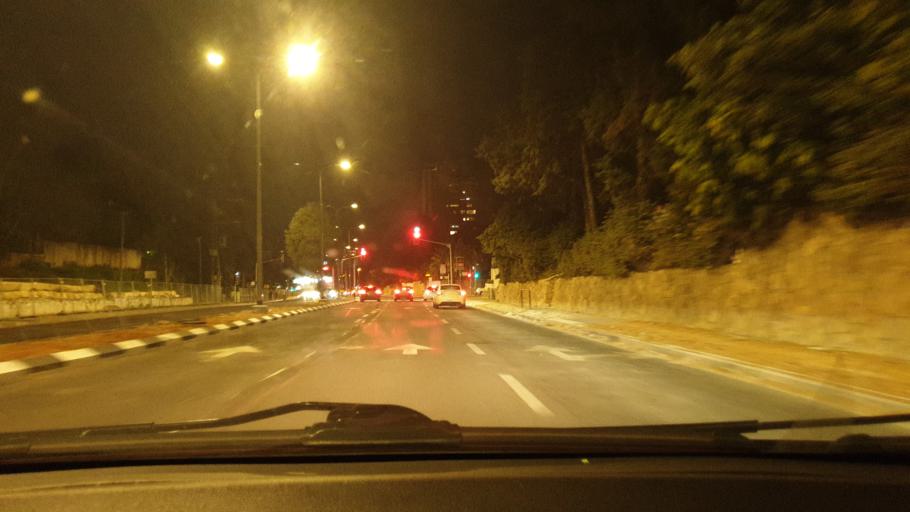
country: IL
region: Tel Aviv
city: Ramat Gan
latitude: 32.1207
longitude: 34.8058
